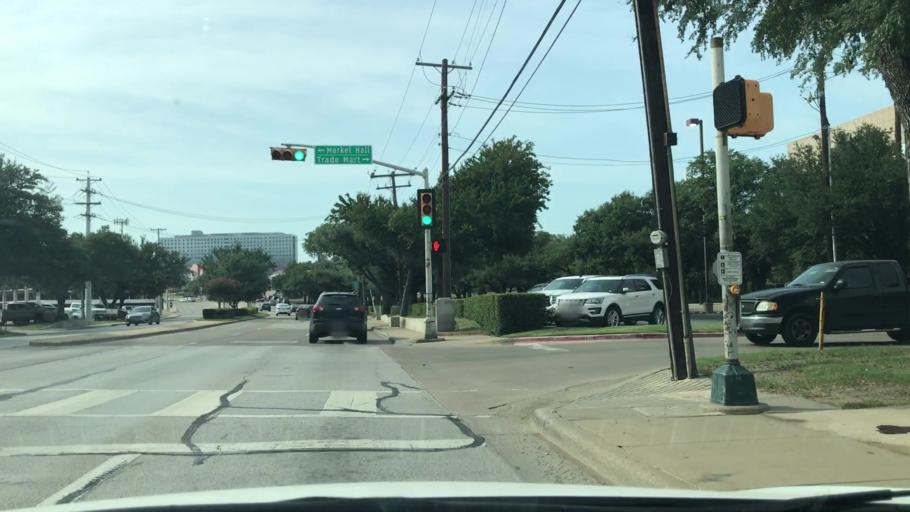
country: US
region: Texas
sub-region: Dallas County
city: Dallas
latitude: 32.8033
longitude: -96.8280
